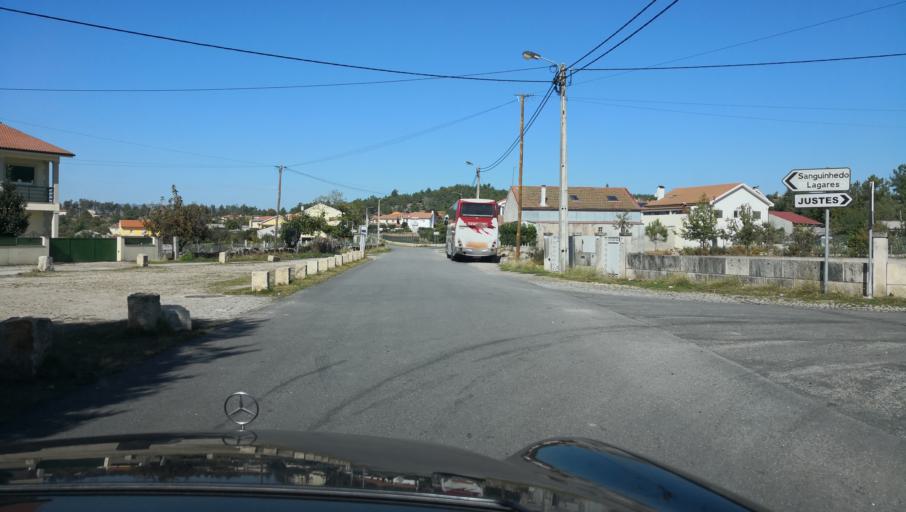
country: PT
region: Vila Real
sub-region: Sabrosa
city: Sabrosa
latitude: 41.3290
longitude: -7.6293
